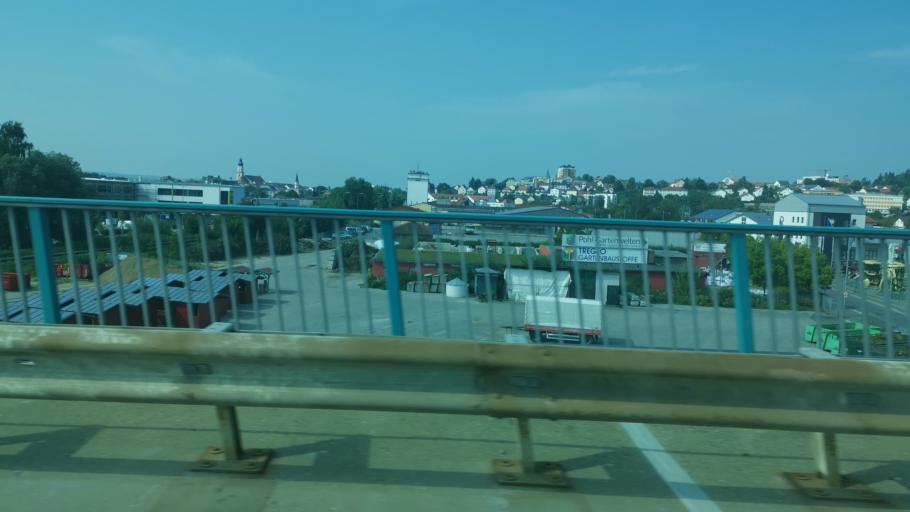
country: DE
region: Bavaria
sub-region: Upper Palatinate
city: Cham
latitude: 49.2237
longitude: 12.6783
